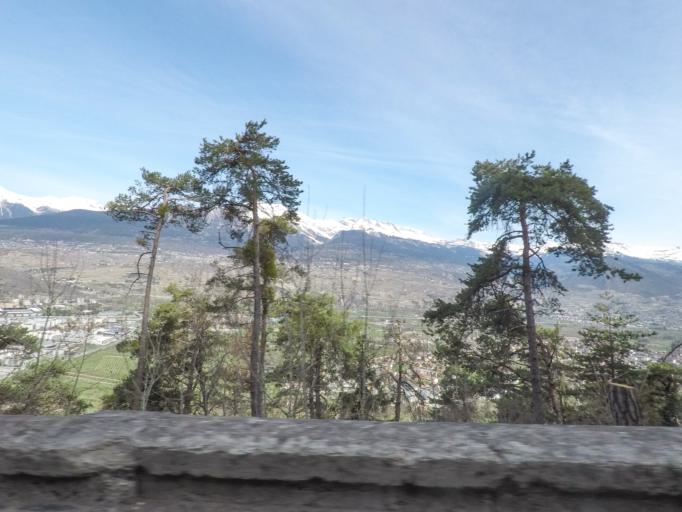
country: CH
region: Valais
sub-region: Herens District
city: Vex
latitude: 46.2228
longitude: 7.3947
